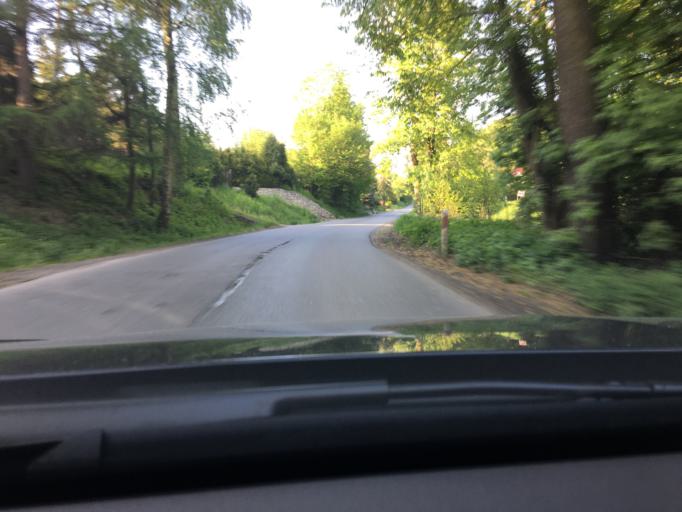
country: PL
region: Lesser Poland Voivodeship
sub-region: Powiat krakowski
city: Jerzmanowice
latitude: 50.2017
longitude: 19.7333
